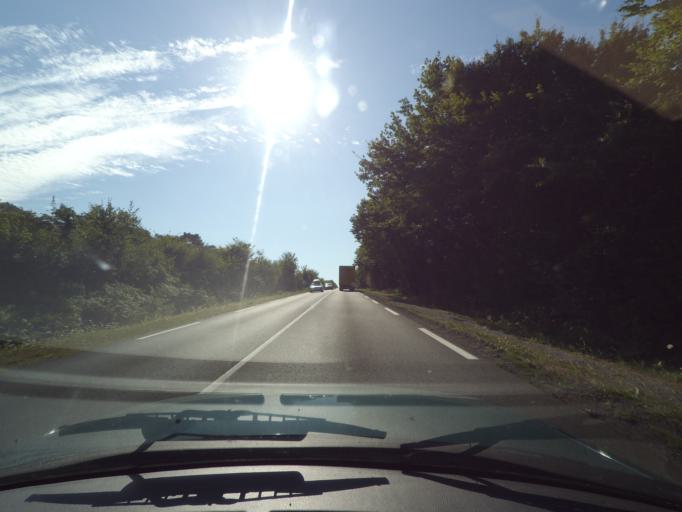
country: FR
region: Poitou-Charentes
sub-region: Departement de la Vienne
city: Terce
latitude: 46.4274
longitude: 0.6200
